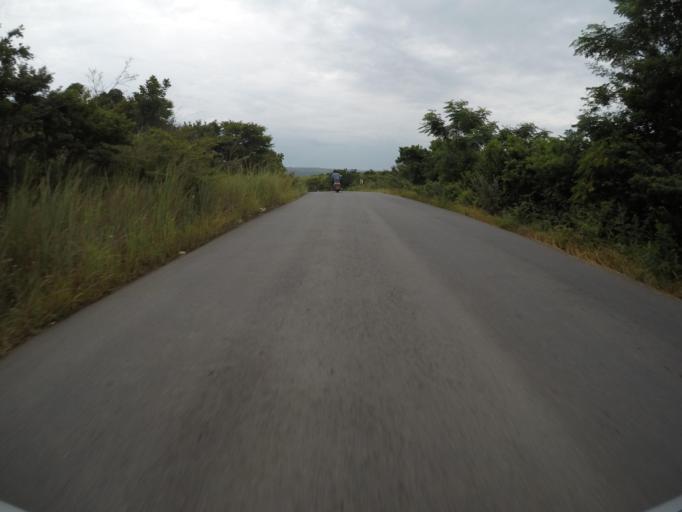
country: ZA
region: Eastern Cape
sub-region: Buffalo City Metropolitan Municipality
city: East London
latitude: -32.9586
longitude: 27.9000
